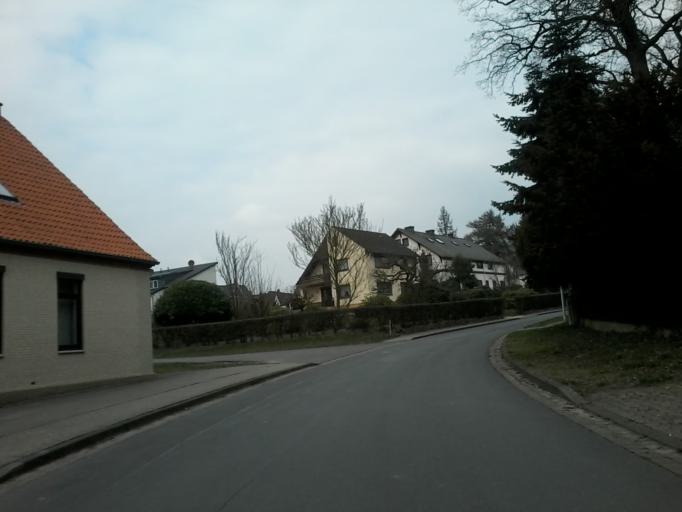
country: DE
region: Lower Saxony
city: Achim
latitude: 52.9982
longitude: 9.0484
